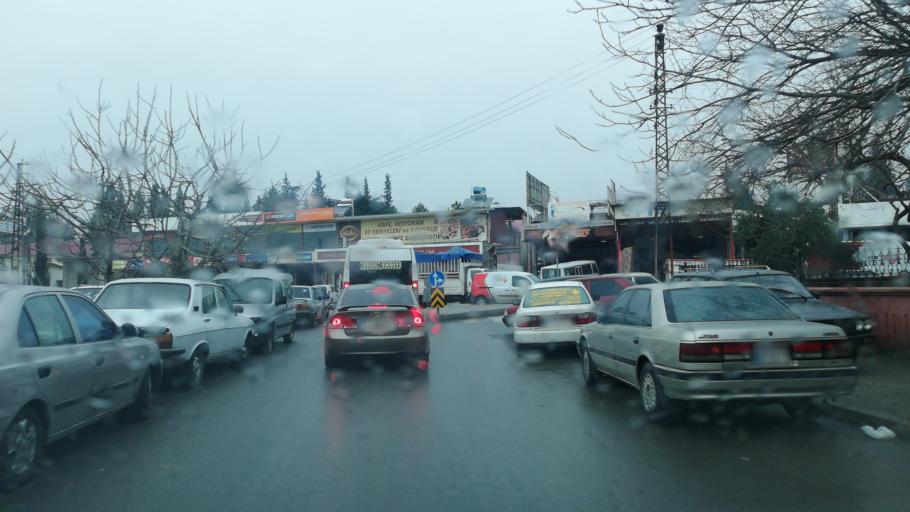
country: TR
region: Kahramanmaras
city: Kahramanmaras
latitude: 37.5651
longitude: 36.9535
